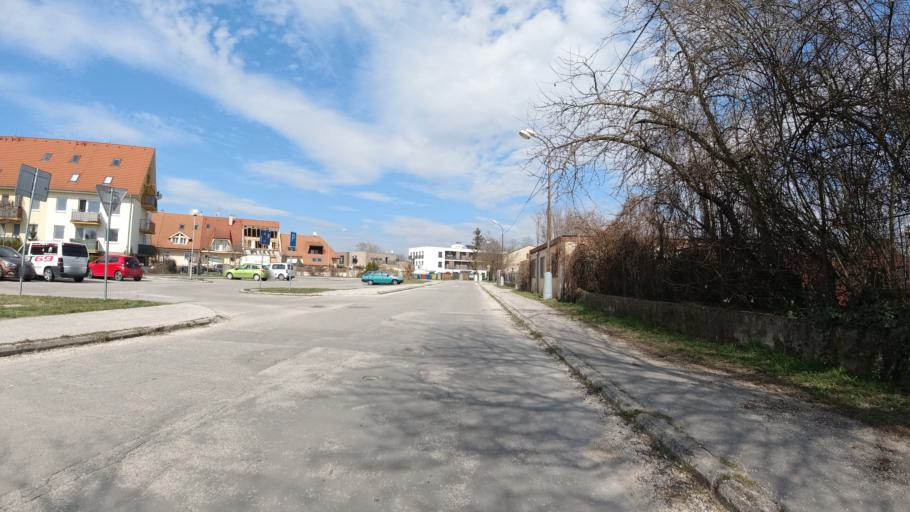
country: SK
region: Trnavsky
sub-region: Okres Trnava
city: Piestany
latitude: 48.6045
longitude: 17.8386
